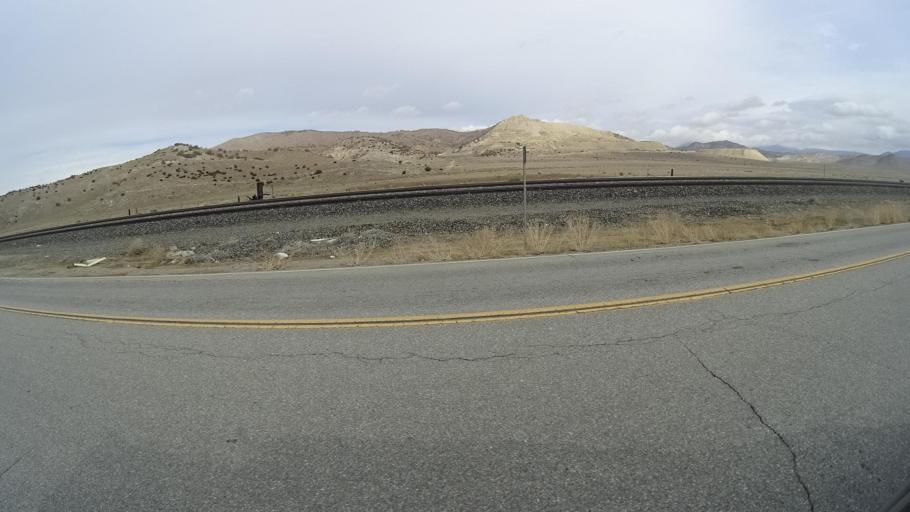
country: US
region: California
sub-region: Kern County
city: Tehachapi
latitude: 35.1259
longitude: -118.4047
